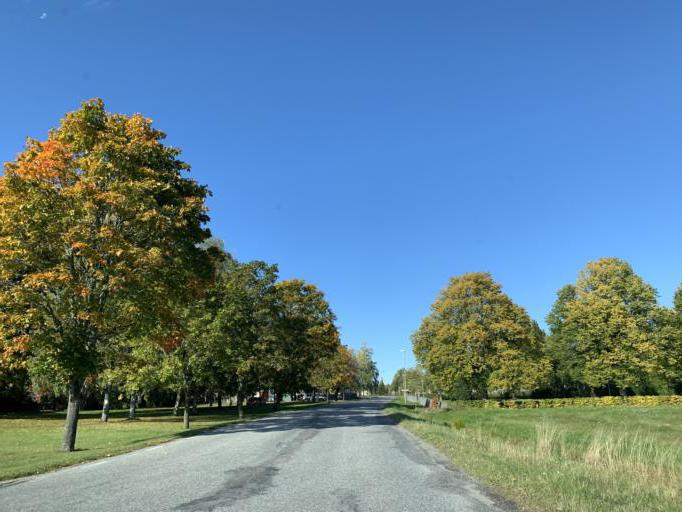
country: SE
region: Soedermanland
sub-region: Eskilstuna Kommun
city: Kvicksund
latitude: 59.5684
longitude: 16.4042
